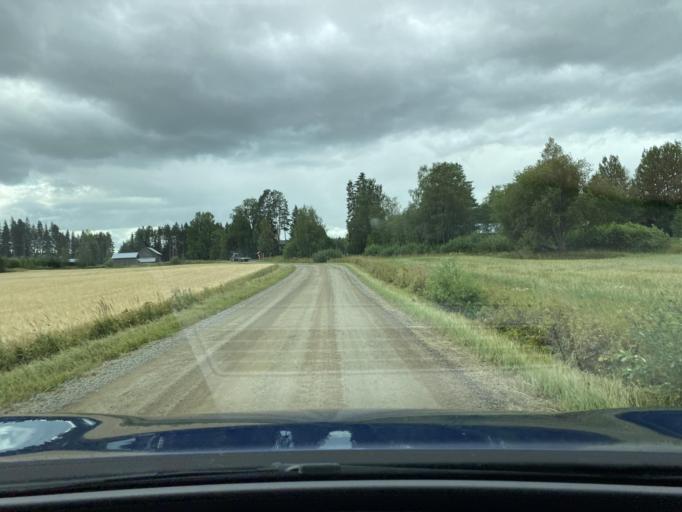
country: FI
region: Pirkanmaa
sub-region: Lounais-Pirkanmaa
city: Punkalaidun
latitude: 61.1814
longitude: 23.1835
